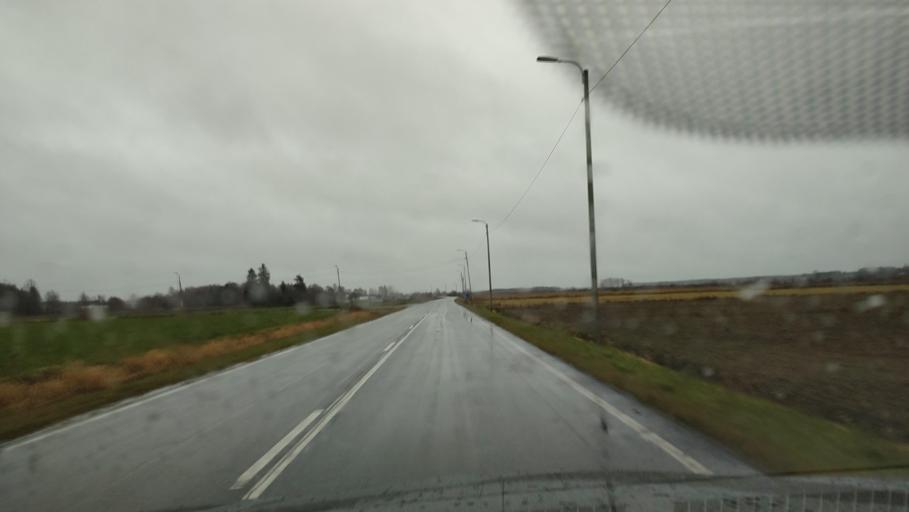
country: FI
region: Ostrobothnia
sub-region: Vaasa
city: Ristinummi
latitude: 63.0467
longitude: 21.7435
